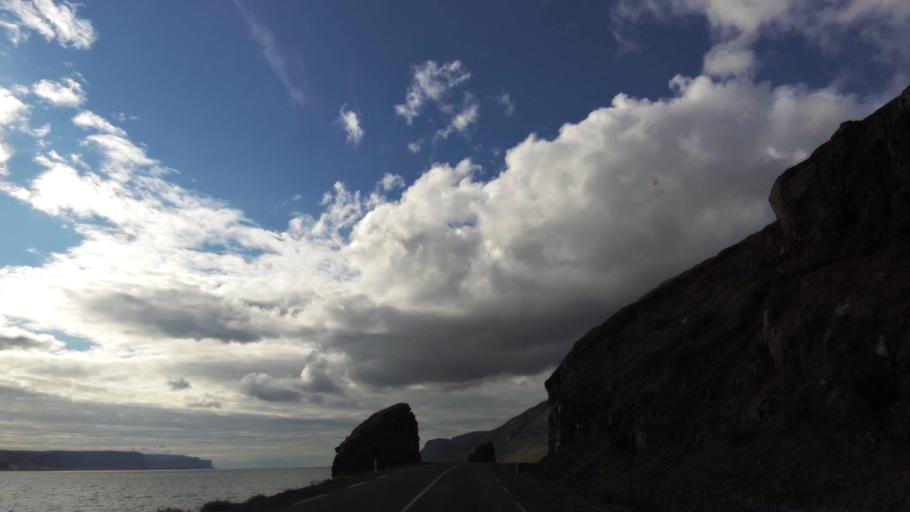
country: IS
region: West
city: Olafsvik
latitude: 65.5449
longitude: -23.8847
